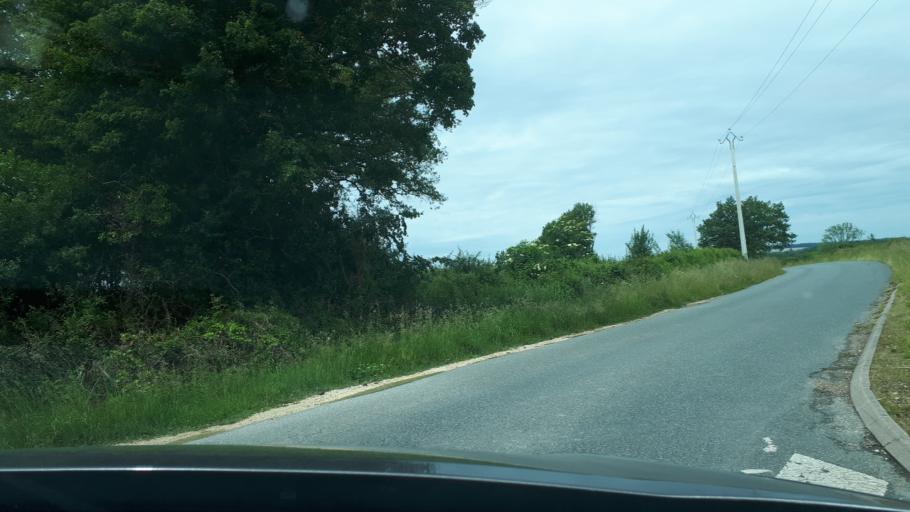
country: FR
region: Centre
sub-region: Departement du Cher
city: Savigny-en-Sancerre
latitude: 47.3946
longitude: 2.6648
